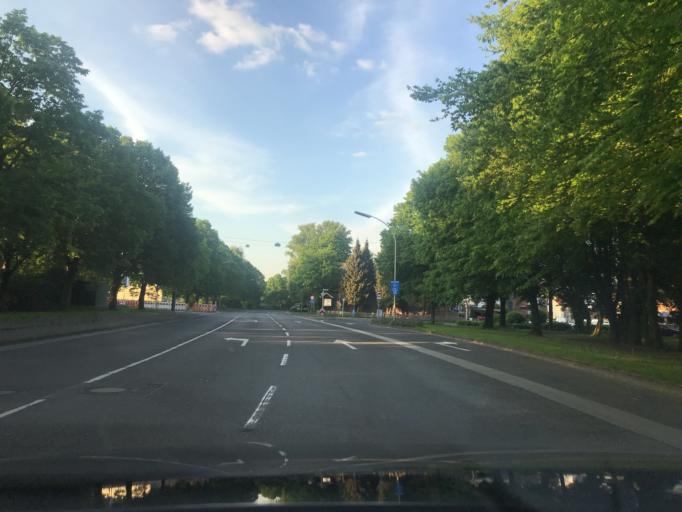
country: DE
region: North Rhine-Westphalia
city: Wegberg
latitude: 51.1453
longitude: 6.3540
